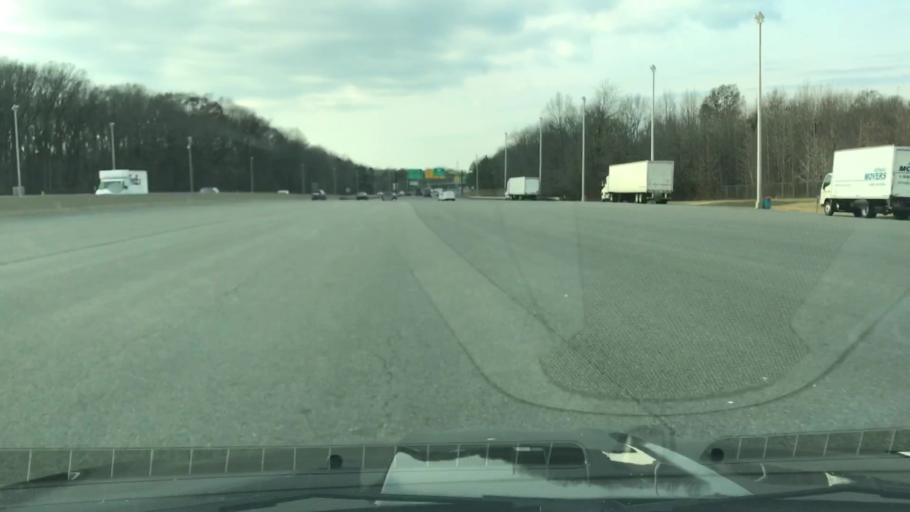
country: US
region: New Jersey
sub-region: Burlington County
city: Roebling
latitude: 40.0969
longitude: -74.7780
